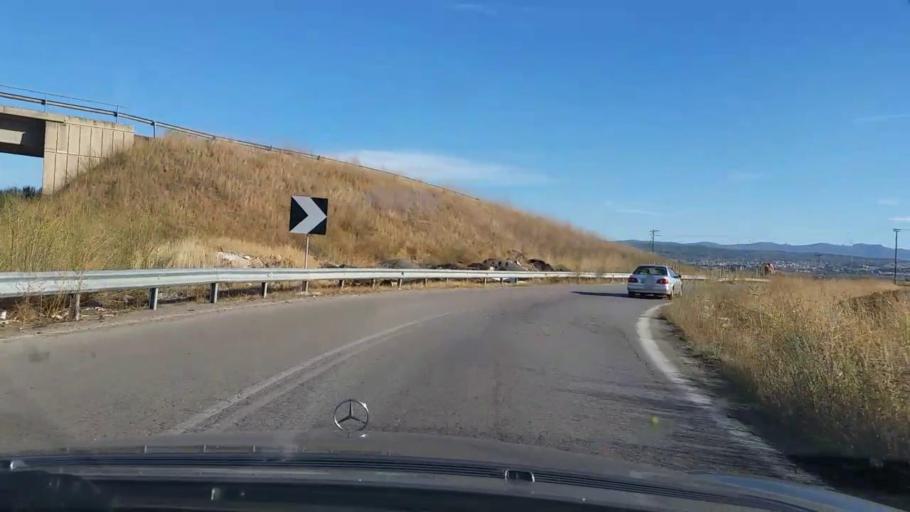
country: GR
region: Central Greece
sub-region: Nomos Voiotias
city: Thivai
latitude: 38.3676
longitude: 23.2999
